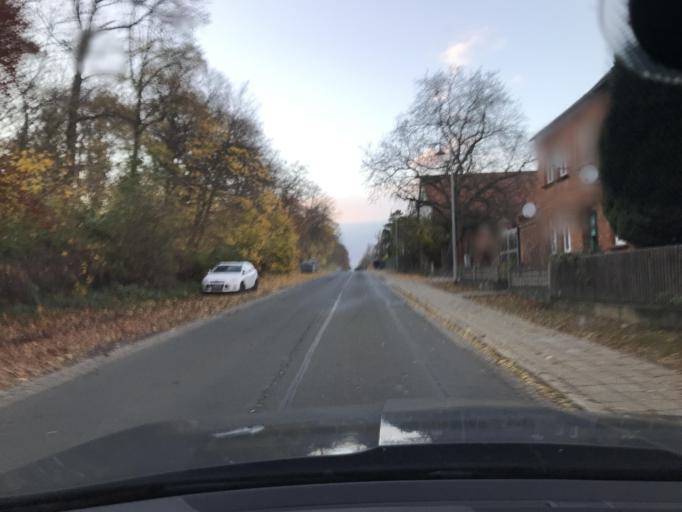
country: DE
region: Saxony-Anhalt
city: Langenstein
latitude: 51.8563
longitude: 10.9865
